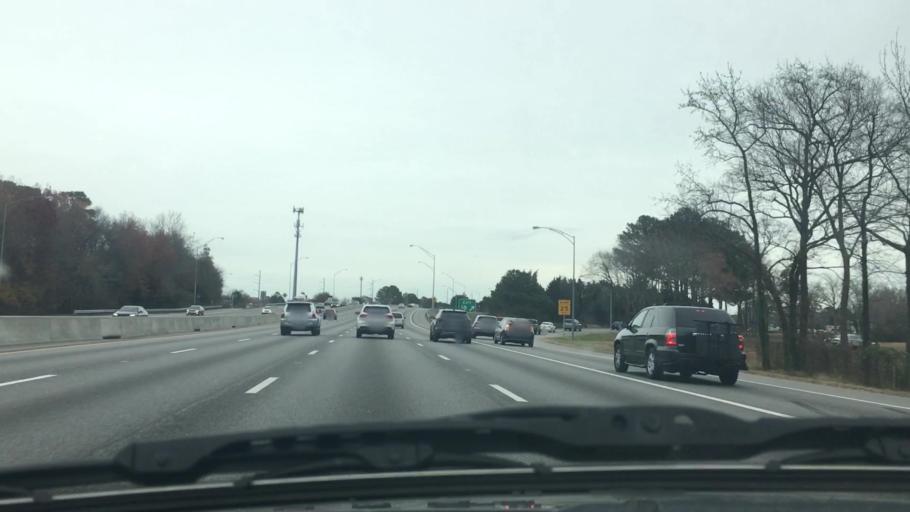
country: US
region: Virginia
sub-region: City of Virginia Beach
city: Virginia Beach
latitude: 36.8369
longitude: -76.1014
